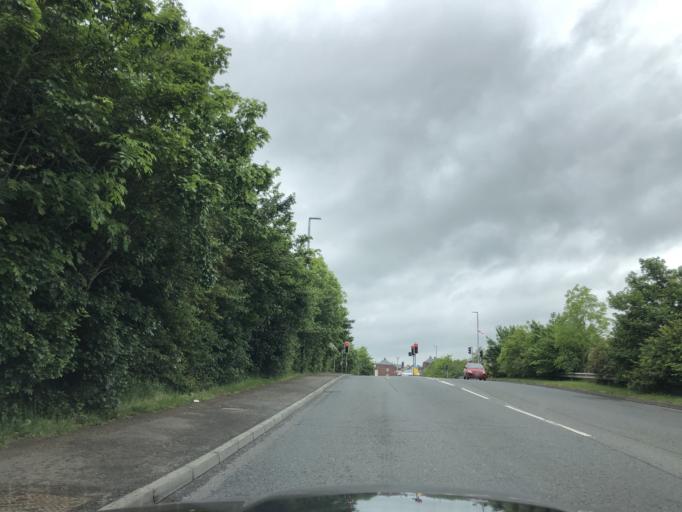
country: GB
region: Northern Ireland
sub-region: Lisburn District
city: Lisburn
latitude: 54.5267
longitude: -6.0730
